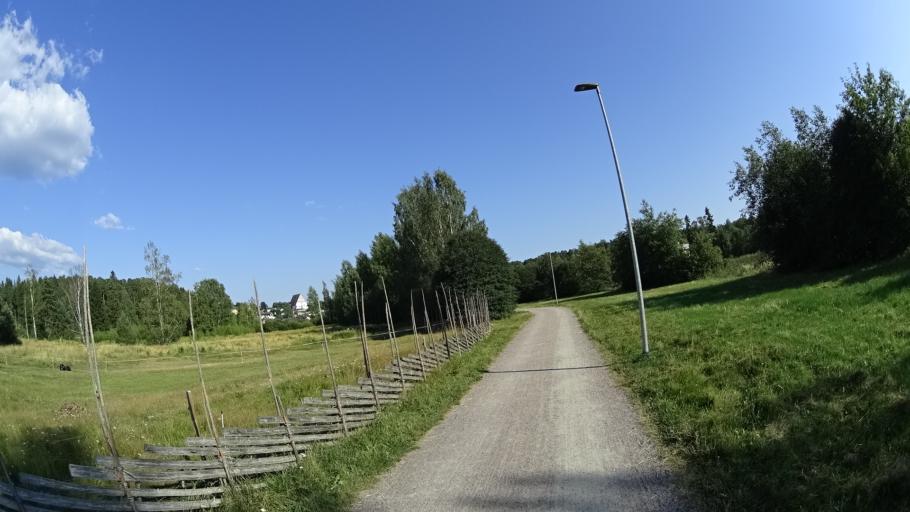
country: FI
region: Uusimaa
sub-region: Porvoo
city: Porvoo
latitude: 60.3989
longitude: 25.6456
